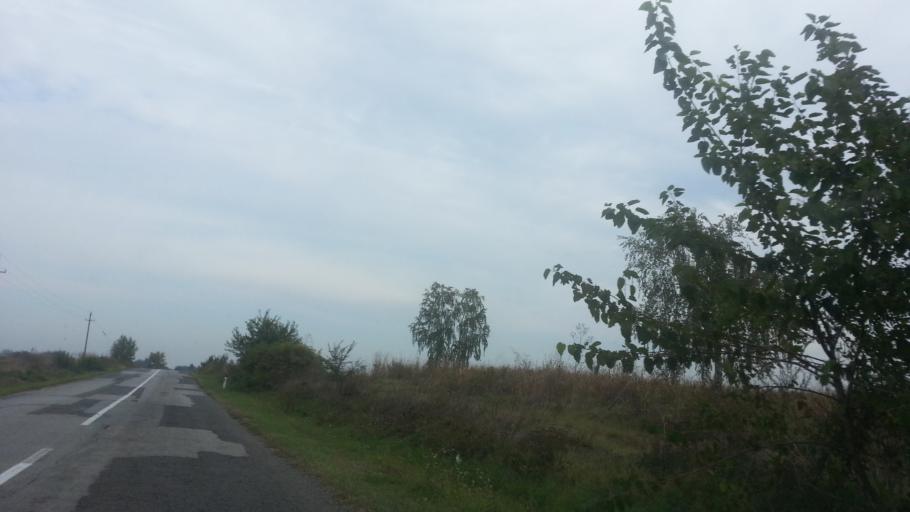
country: RS
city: Surduk
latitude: 45.0562
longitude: 20.3312
